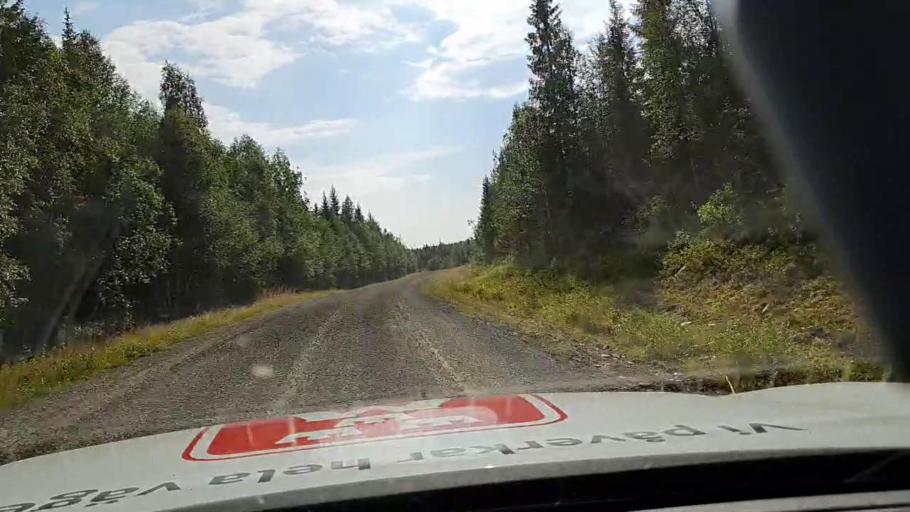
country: SE
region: Vaesterbotten
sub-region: Storumans Kommun
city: Fristad
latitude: 65.5427
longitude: 16.7971
